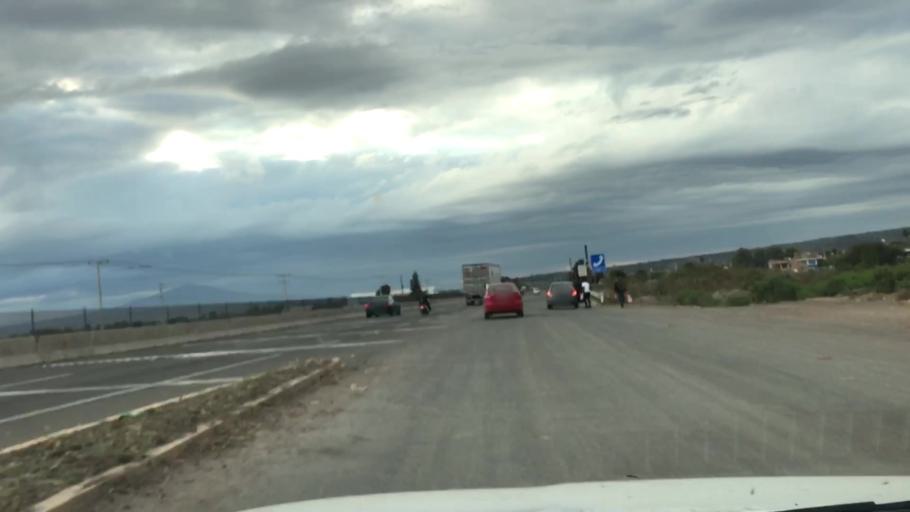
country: MX
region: Guanajuato
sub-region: Penjamo
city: Estacion la Piedad
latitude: 20.3888
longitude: -101.9362
